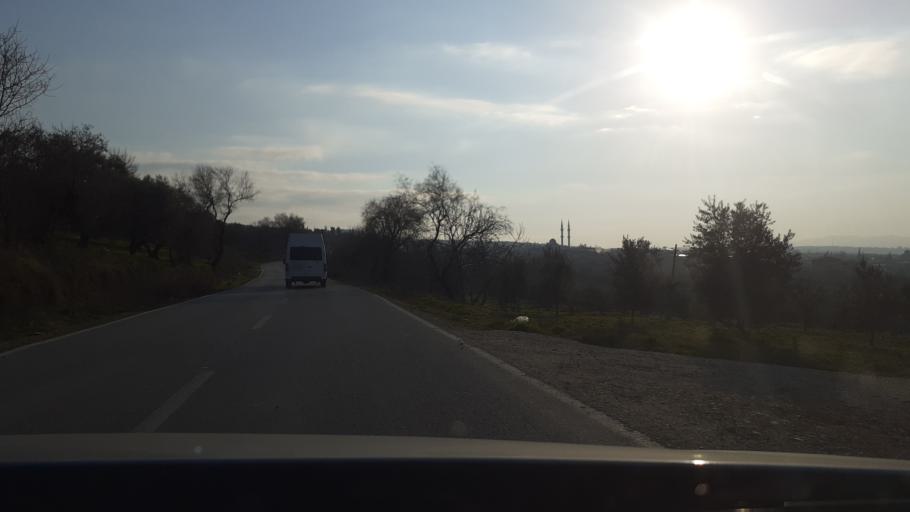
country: TR
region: Hatay
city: Oymakli
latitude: 36.1174
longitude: 36.3039
